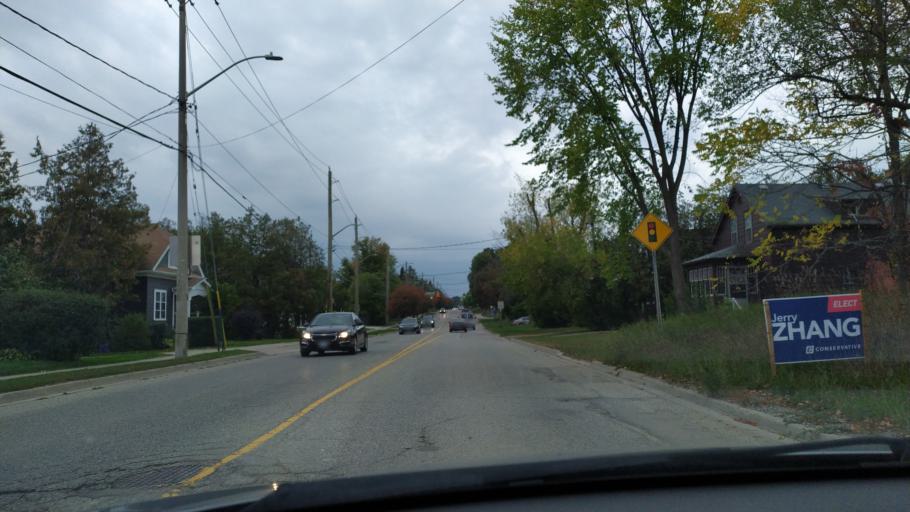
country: CA
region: Ontario
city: Waterloo
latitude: 43.4841
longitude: -80.4867
